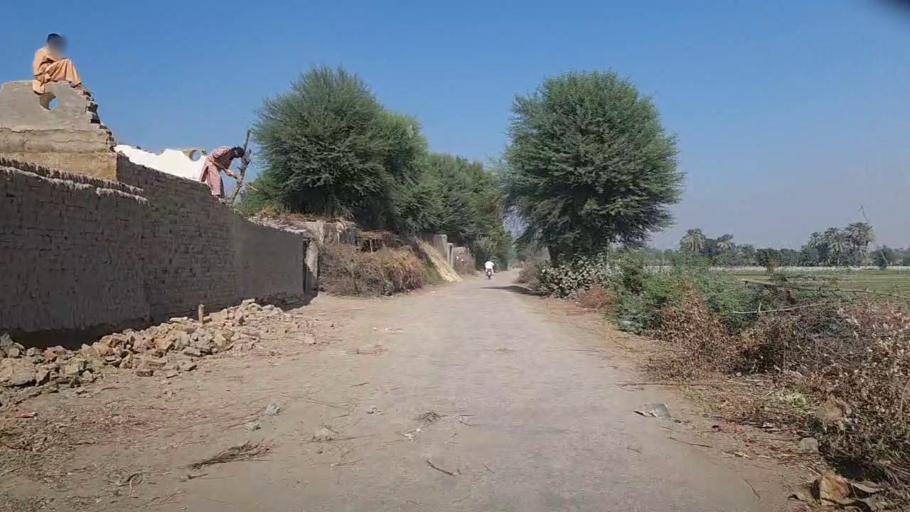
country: PK
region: Sindh
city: Bozdar
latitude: 27.1997
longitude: 68.6649
